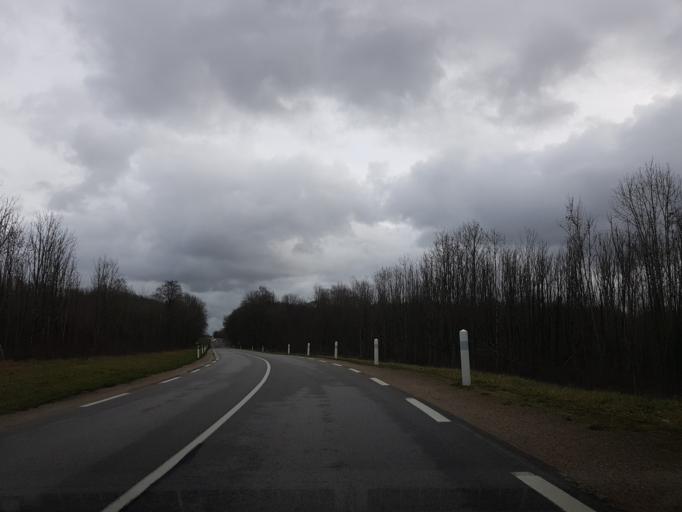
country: FR
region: Champagne-Ardenne
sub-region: Departement de la Haute-Marne
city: Fayl-Billot
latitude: 47.7964
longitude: 5.5647
